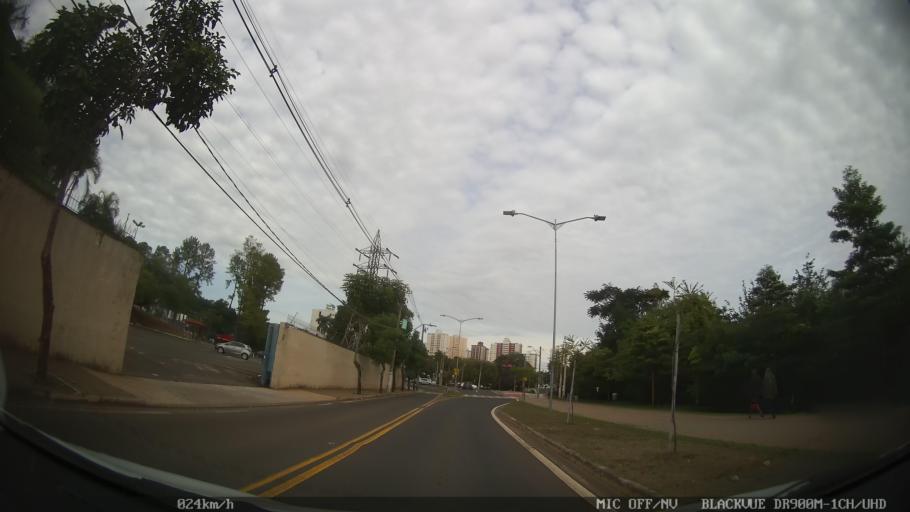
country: BR
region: Sao Paulo
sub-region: Piracicaba
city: Piracicaba
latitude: -22.7142
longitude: -47.6500
